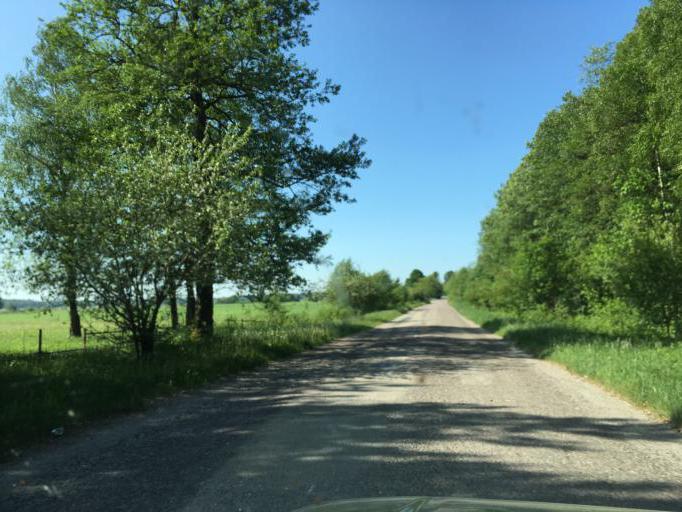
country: LV
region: Ventspils
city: Ventspils
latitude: 57.5030
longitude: 21.8461
